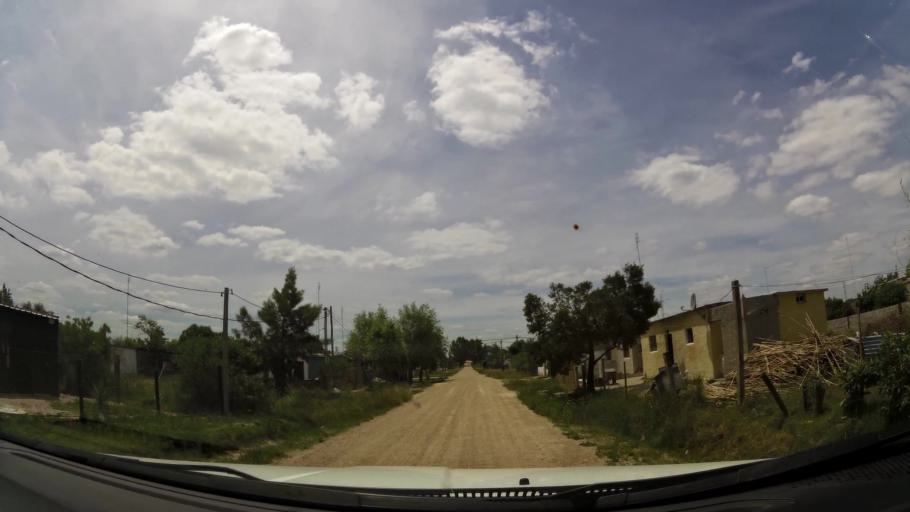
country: UY
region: San Jose
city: Delta del Tigre
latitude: -34.7600
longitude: -56.4113
